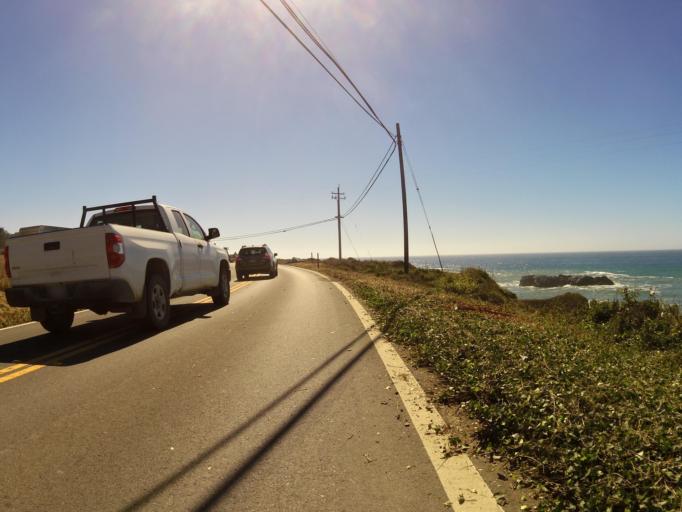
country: US
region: California
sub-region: Mendocino County
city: Fort Bragg
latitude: 39.6474
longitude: -123.7841
